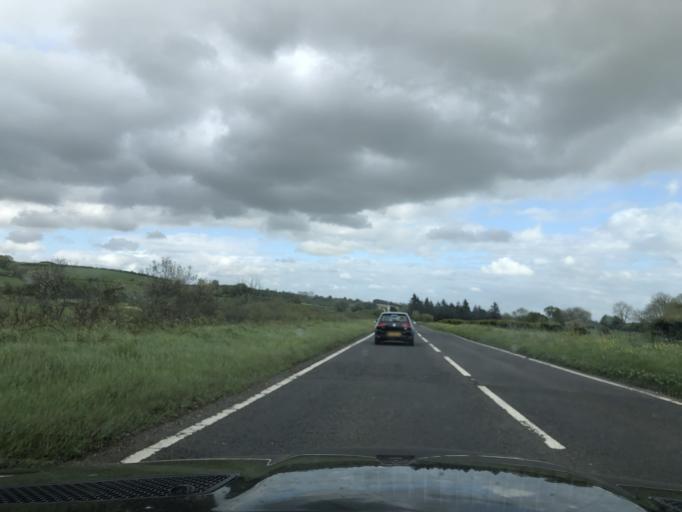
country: GB
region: Northern Ireland
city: Dunloy
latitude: 55.0207
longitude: -6.3781
